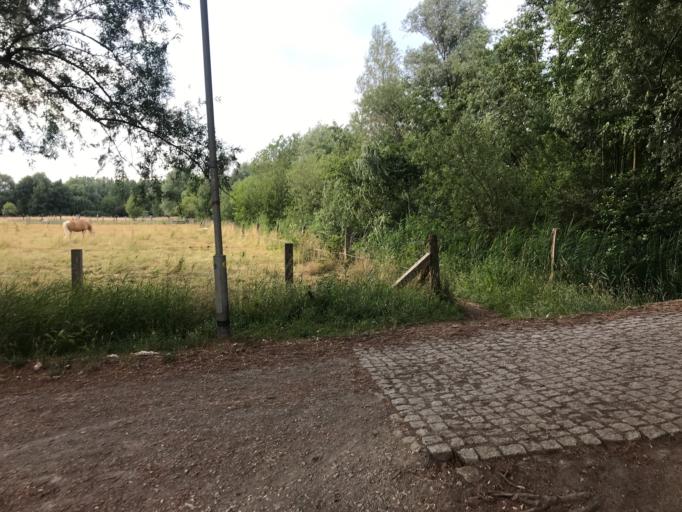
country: DE
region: Lower Saxony
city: Isernhagen Farster Bauerschaft
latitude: 52.4215
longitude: 9.8169
